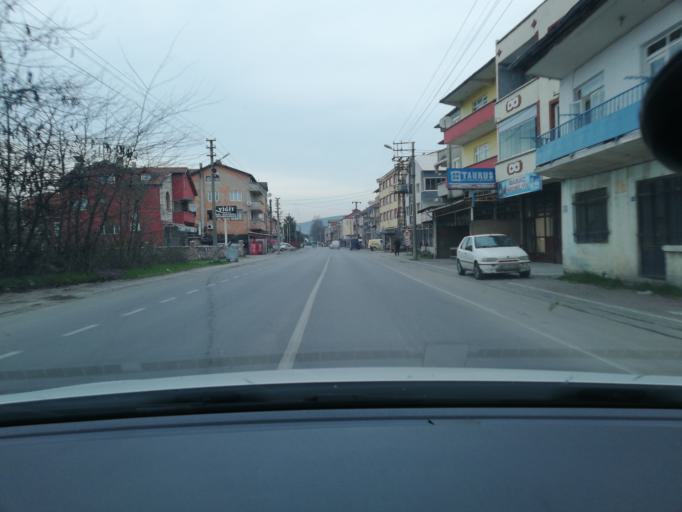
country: TR
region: Zonguldak
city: Caycuma
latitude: 41.4188
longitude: 32.0941
